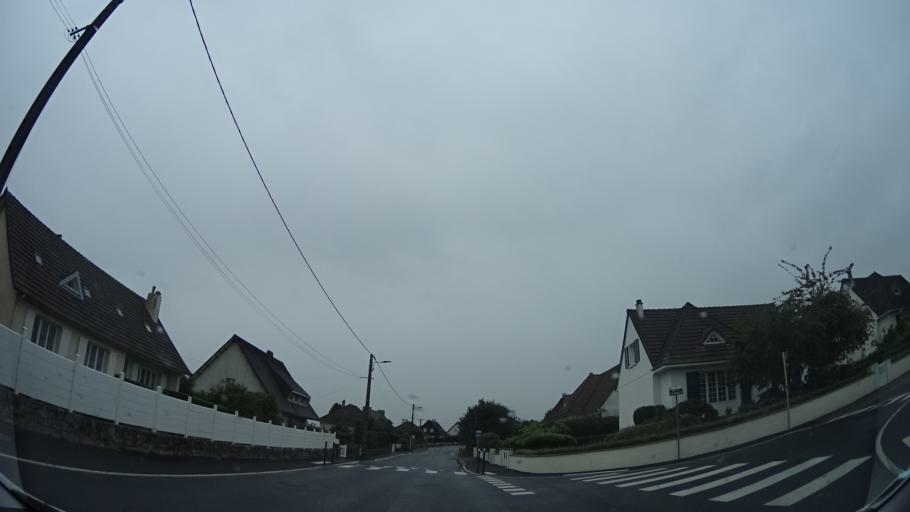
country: FR
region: Lower Normandy
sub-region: Departement de la Manche
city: Octeville
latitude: 49.6235
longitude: -1.6517
